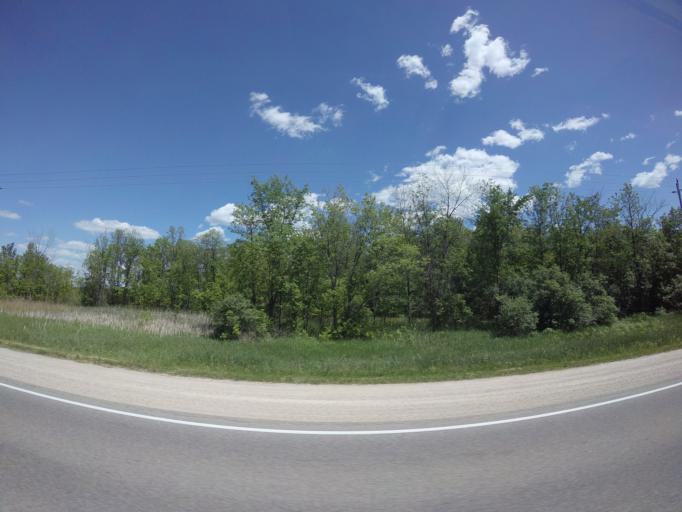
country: CA
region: Ontario
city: Perth
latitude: 44.9486
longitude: -76.2365
